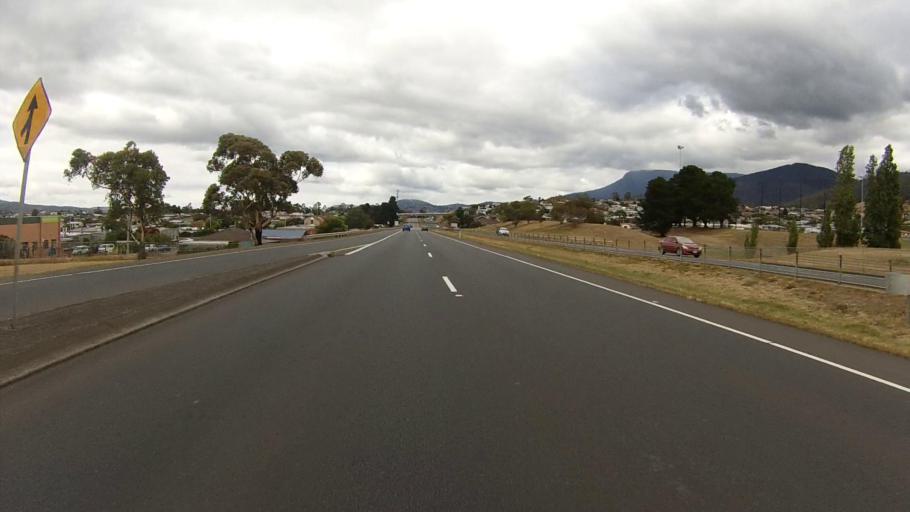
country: AU
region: Tasmania
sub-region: Glenorchy
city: Claremont
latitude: -42.7891
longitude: 147.2450
